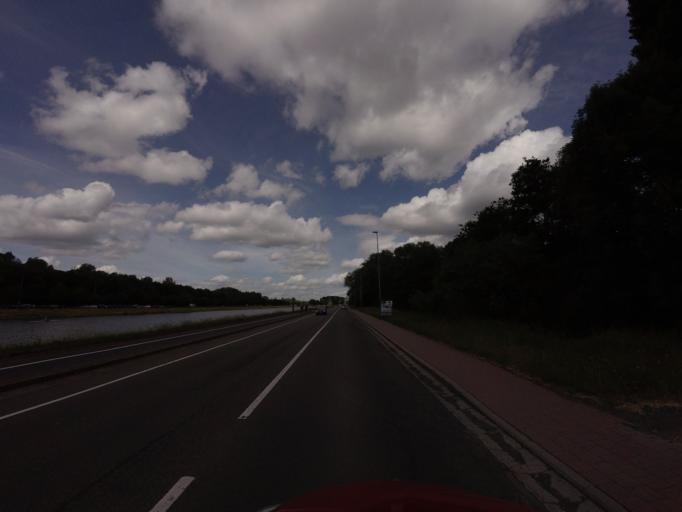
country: BE
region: Flanders
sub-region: Provincie Oost-Vlaanderen
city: Gent
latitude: 51.0514
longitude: 3.6835
